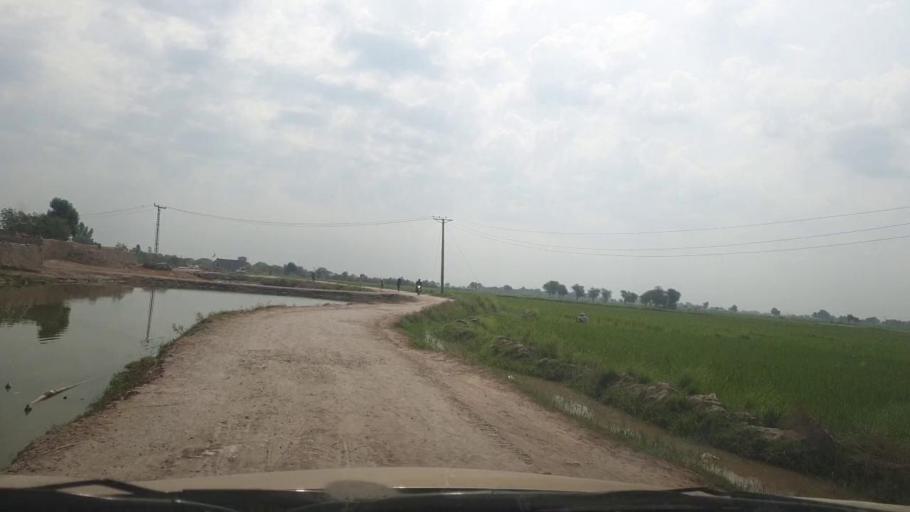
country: PK
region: Sindh
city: Larkana
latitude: 27.6516
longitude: 68.1990
